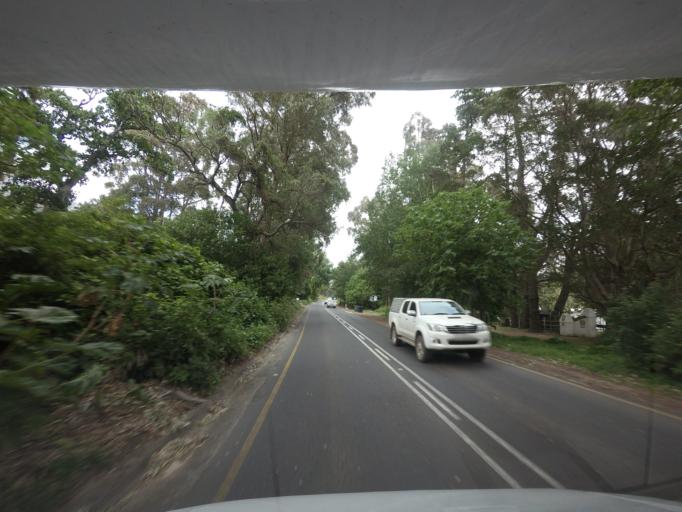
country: ZA
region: Western Cape
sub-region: City of Cape Town
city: Constantia
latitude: -34.0147
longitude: 18.3853
